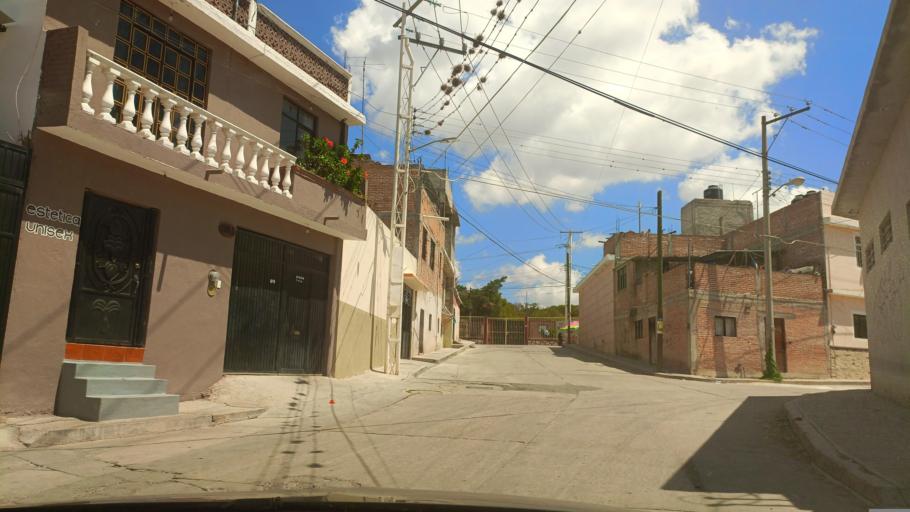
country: MX
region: Guanajuato
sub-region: San Luis de la Paz
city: San Luis de la Paz
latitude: 21.3016
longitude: -100.5053
